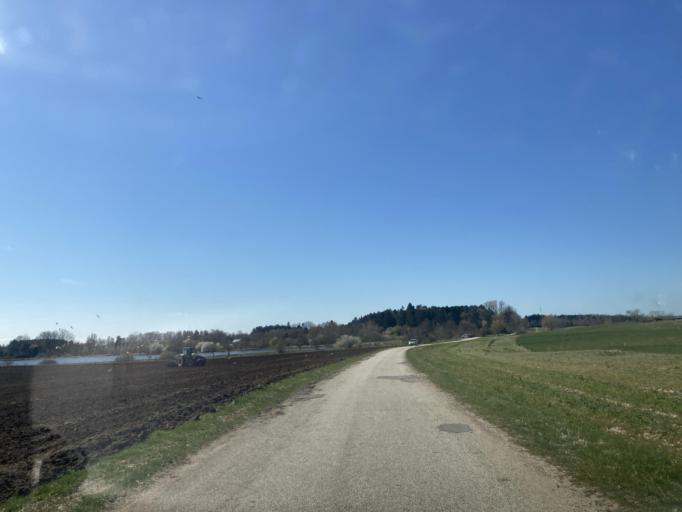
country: DK
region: Capital Region
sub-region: Gribskov Kommune
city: Helsinge
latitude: 55.9995
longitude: 12.2555
